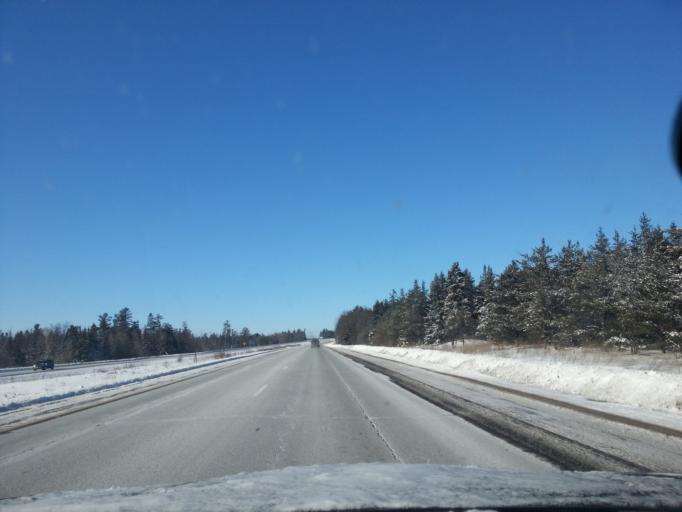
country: CA
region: Ontario
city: Carleton Place
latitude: 45.3343
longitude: -76.1692
